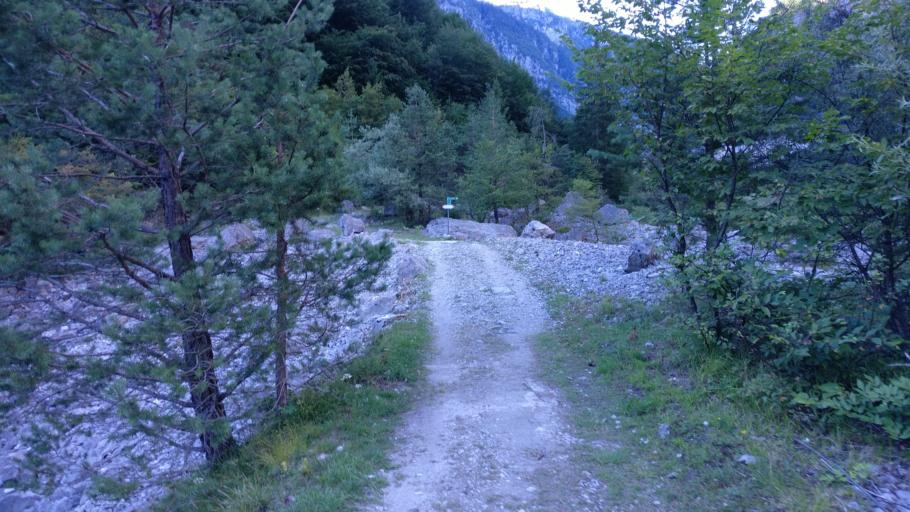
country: IT
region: Trentino-Alto Adige
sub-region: Provincia di Trento
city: Terres
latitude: 46.2881
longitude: 10.9734
